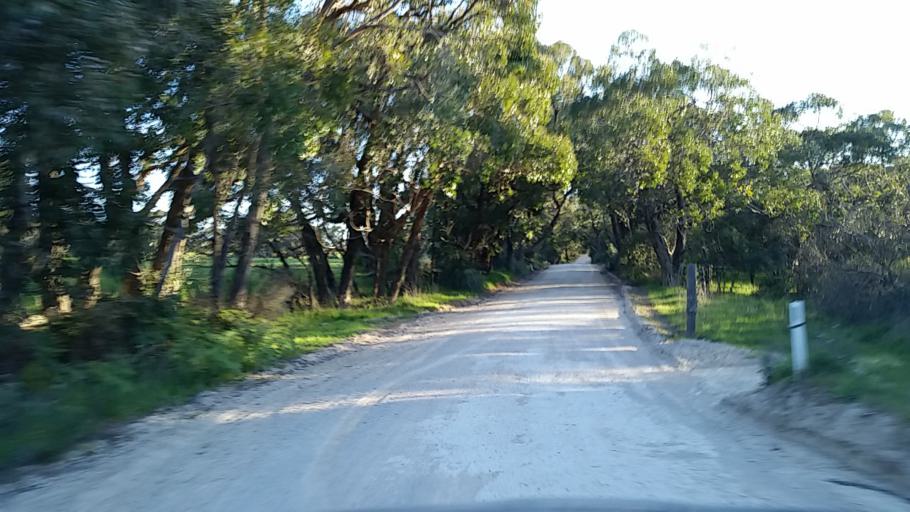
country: AU
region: South Australia
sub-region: Alexandrina
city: Mount Compass
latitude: -35.3096
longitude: 138.6725
